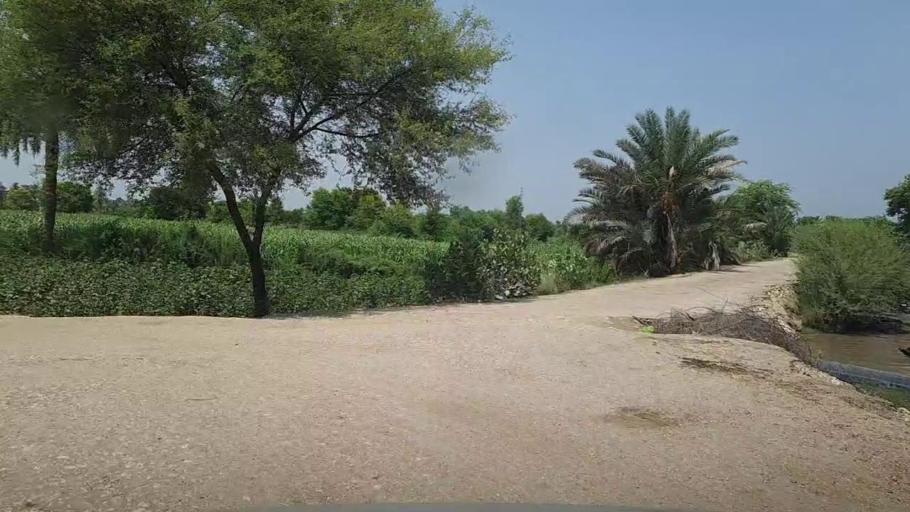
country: PK
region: Sindh
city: Pano Aqil
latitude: 27.8556
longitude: 69.1337
